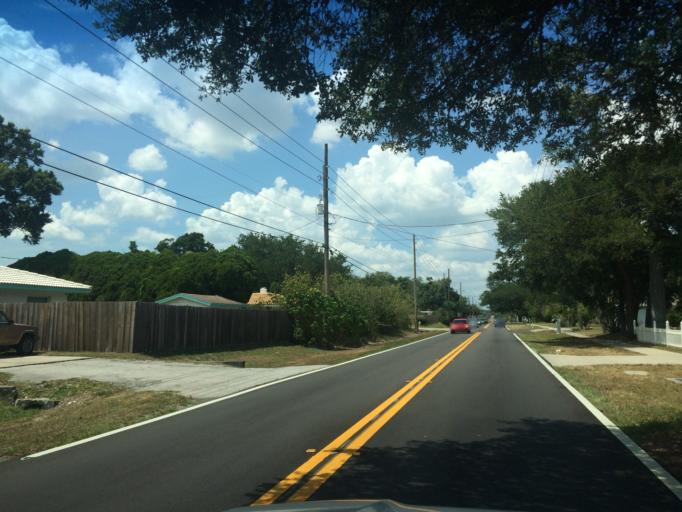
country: US
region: Florida
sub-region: Pinellas County
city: Clearwater
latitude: 27.9466
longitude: -82.7751
